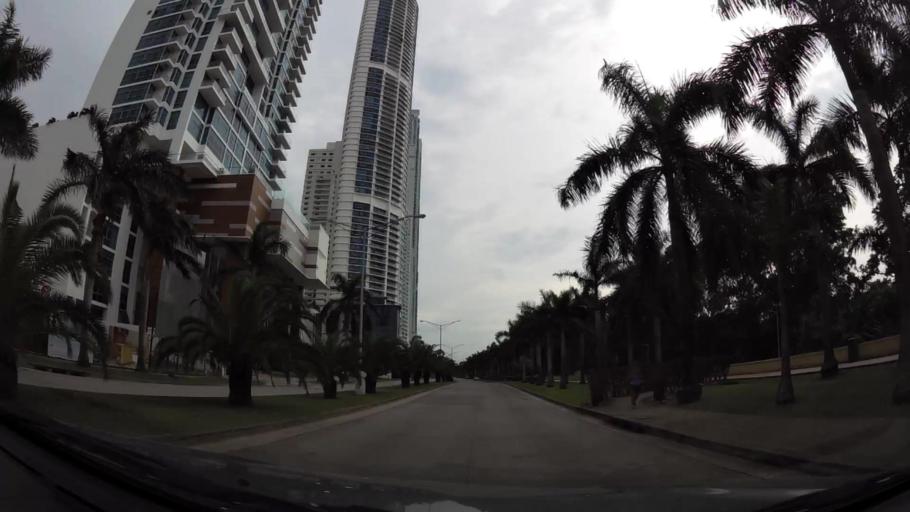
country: PA
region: Panama
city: San Miguelito
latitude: 9.0097
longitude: -79.4676
